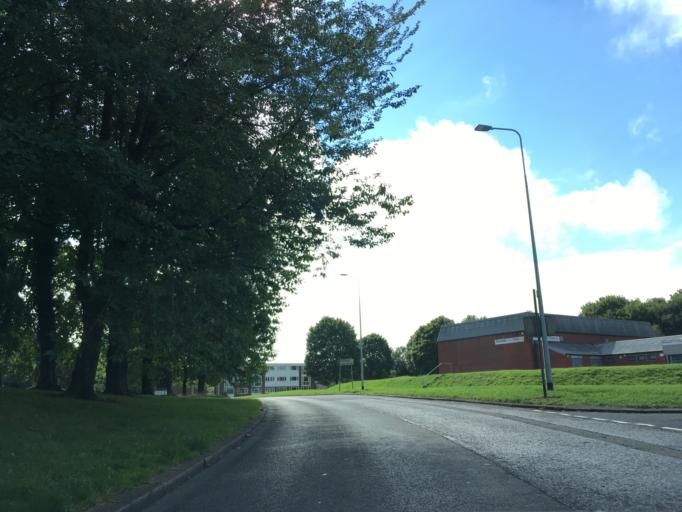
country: GB
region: Wales
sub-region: Cardiff
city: Cardiff
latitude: 51.5186
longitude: -3.1553
